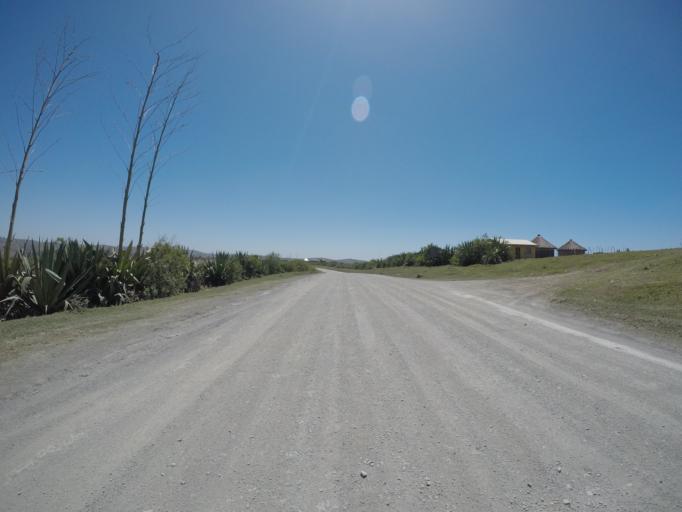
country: ZA
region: Eastern Cape
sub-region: OR Tambo District Municipality
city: Libode
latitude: -32.0091
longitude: 29.0735
